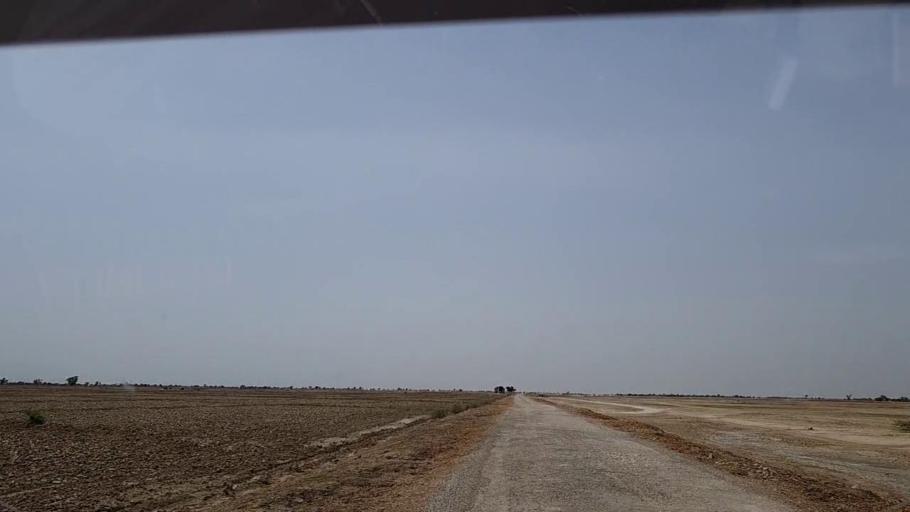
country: PK
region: Sindh
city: Johi
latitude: 26.7273
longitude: 67.6406
